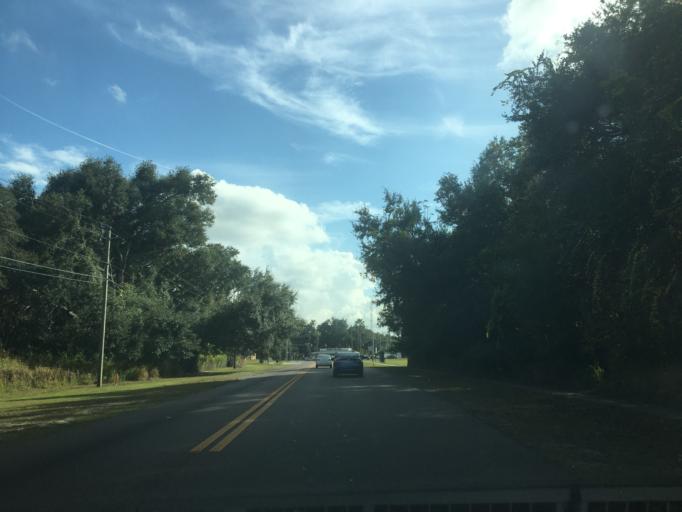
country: US
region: Florida
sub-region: Hillsborough County
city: Temple Terrace
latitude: 28.0126
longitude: -82.4307
